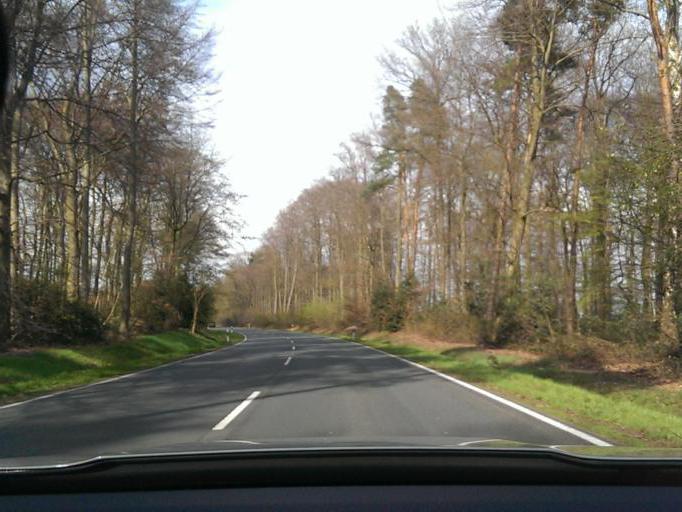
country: DE
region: North Rhine-Westphalia
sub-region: Regierungsbezirk Detmold
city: Hovelhof
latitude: 51.7888
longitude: 8.6190
